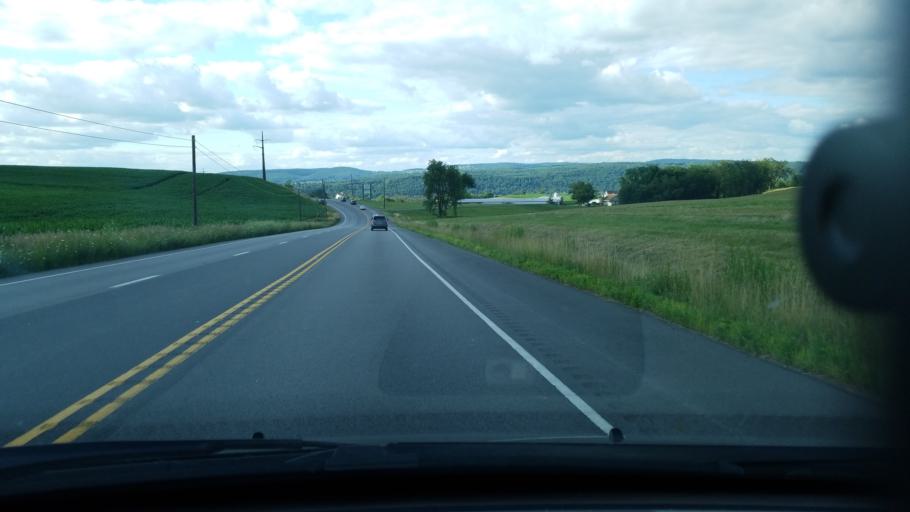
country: US
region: Pennsylvania
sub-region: Montour County
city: Mechanicsville
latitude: 40.9169
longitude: -76.5859
